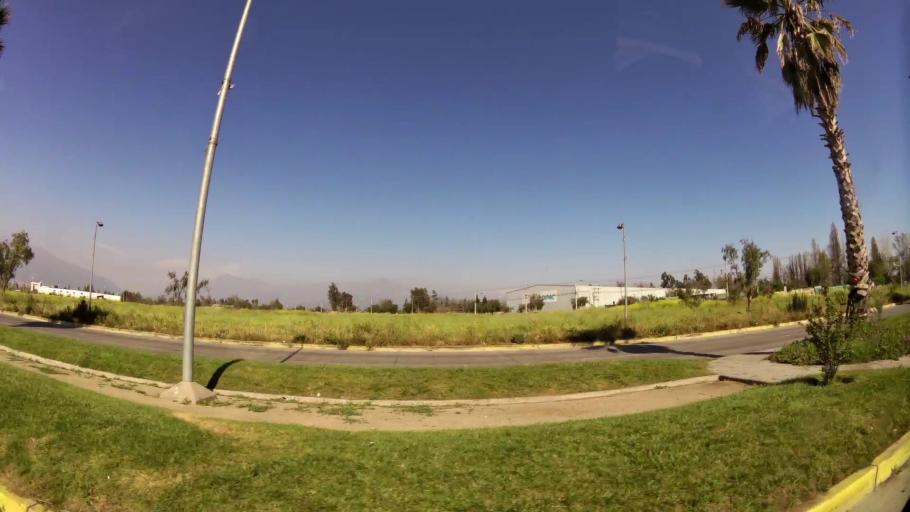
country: CL
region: Santiago Metropolitan
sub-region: Provincia de Santiago
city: La Pintana
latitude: -33.5874
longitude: -70.6342
